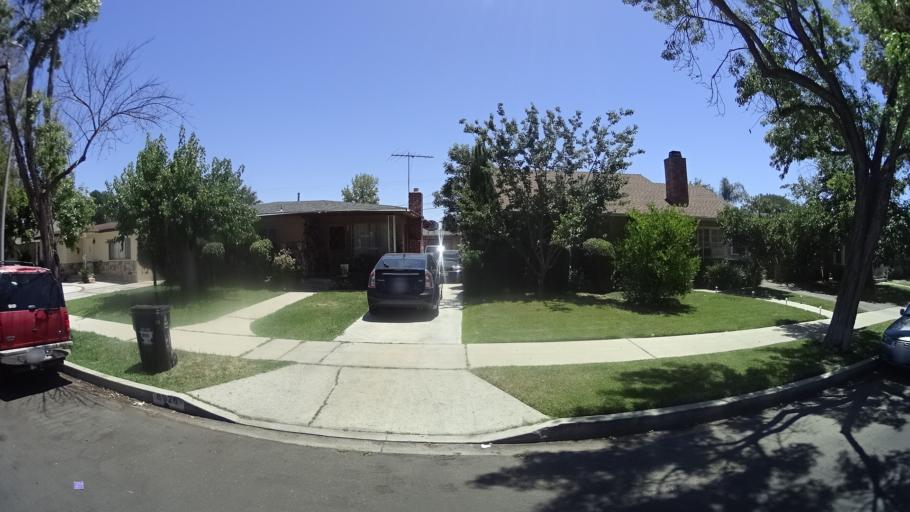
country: US
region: California
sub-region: Los Angeles County
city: Northridge
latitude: 34.1963
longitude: -118.5295
